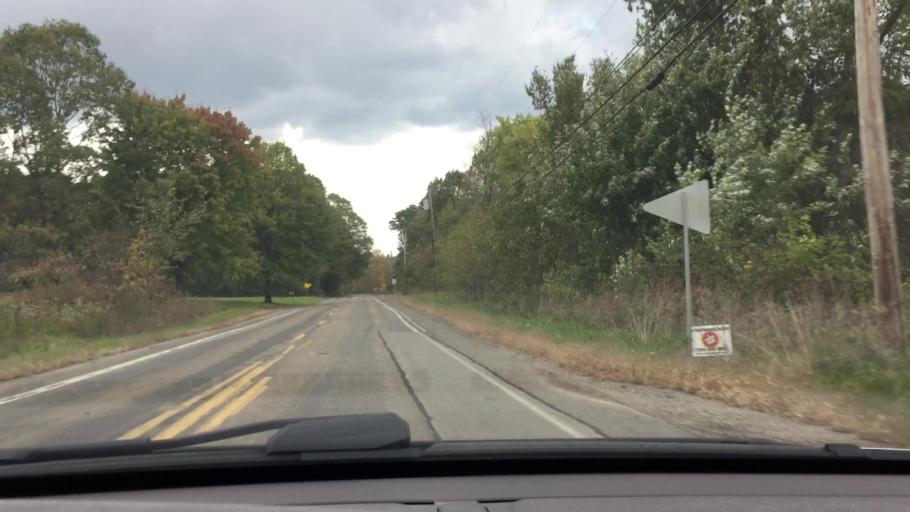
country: US
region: Pennsylvania
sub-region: Lawrence County
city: Oakwood
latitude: 41.0425
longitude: -80.4402
